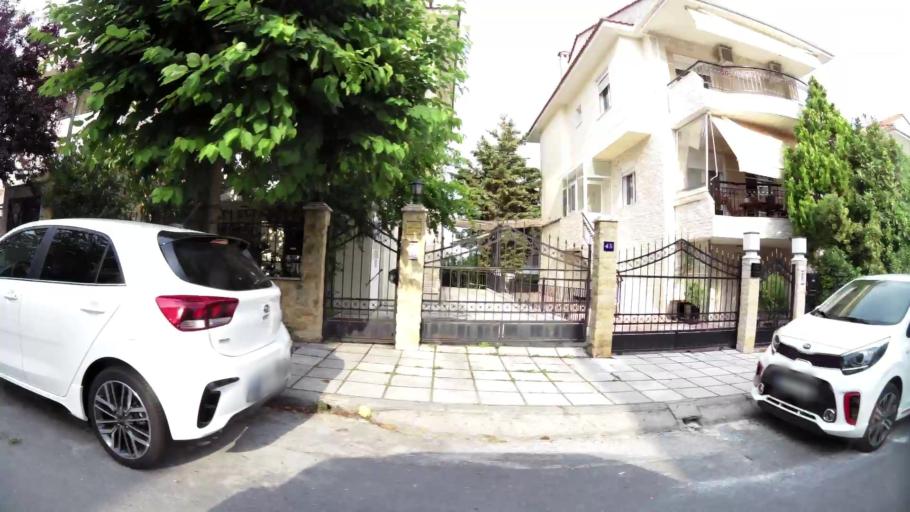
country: GR
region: Central Macedonia
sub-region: Nomos Thessalonikis
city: Oraiokastro
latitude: 40.7256
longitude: 22.9172
